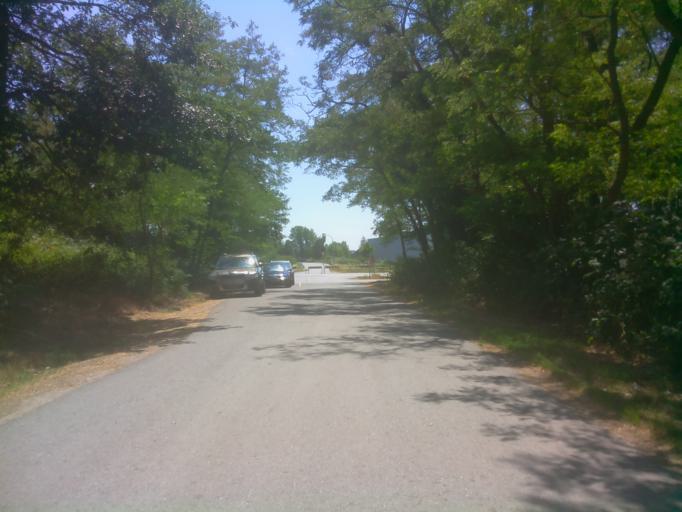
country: DE
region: Hesse
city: Lorsch
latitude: 49.6673
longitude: 8.5648
